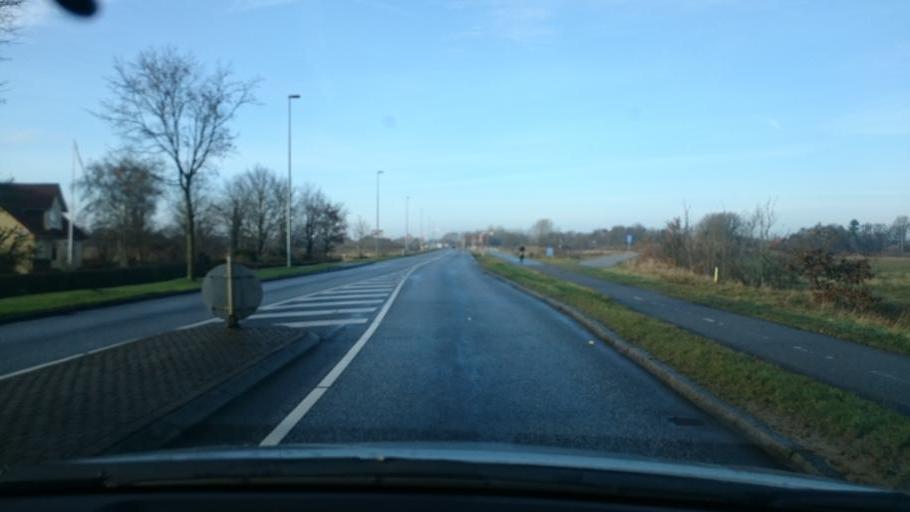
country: DK
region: South Denmark
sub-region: Esbjerg Kommune
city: Ribe
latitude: 55.3187
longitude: 8.7698
